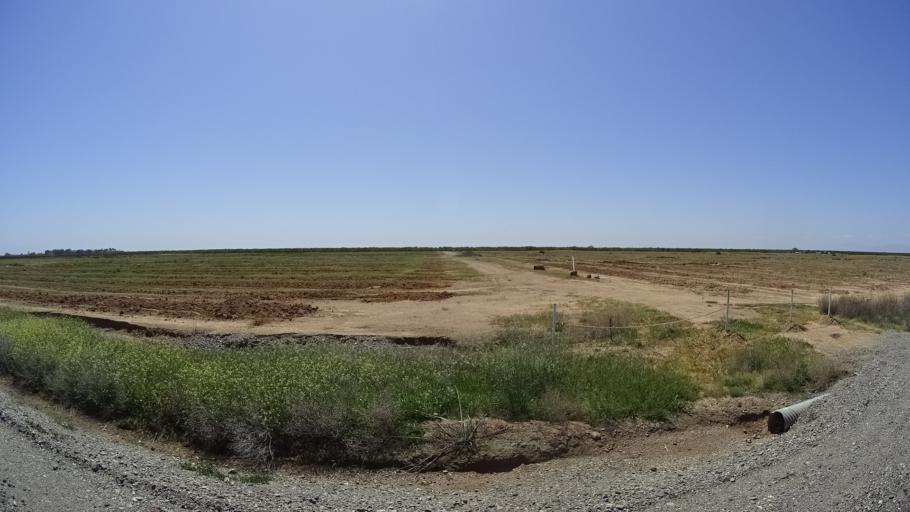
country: US
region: California
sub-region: Glenn County
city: Hamilton City
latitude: 39.7665
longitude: -122.0647
